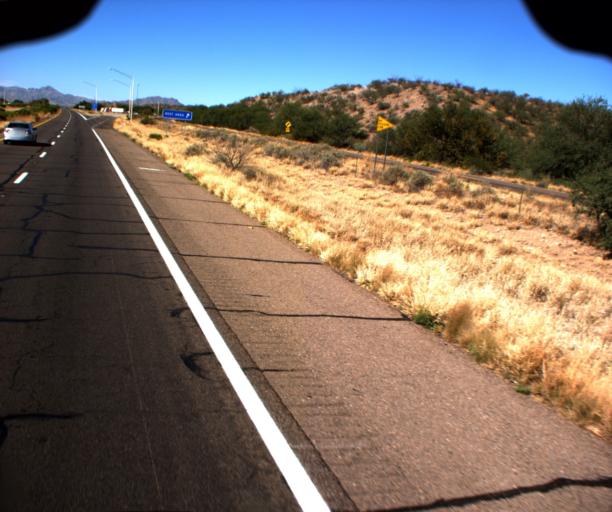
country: US
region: Arizona
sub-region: Pima County
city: Arivaca Junction
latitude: 31.7757
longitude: -111.0308
